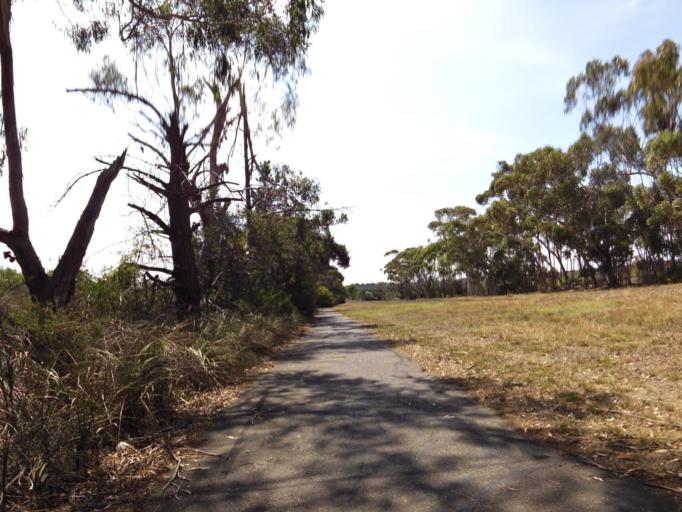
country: AU
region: Victoria
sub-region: Mornington Peninsula
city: Hastings
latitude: -38.3275
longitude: 145.1831
